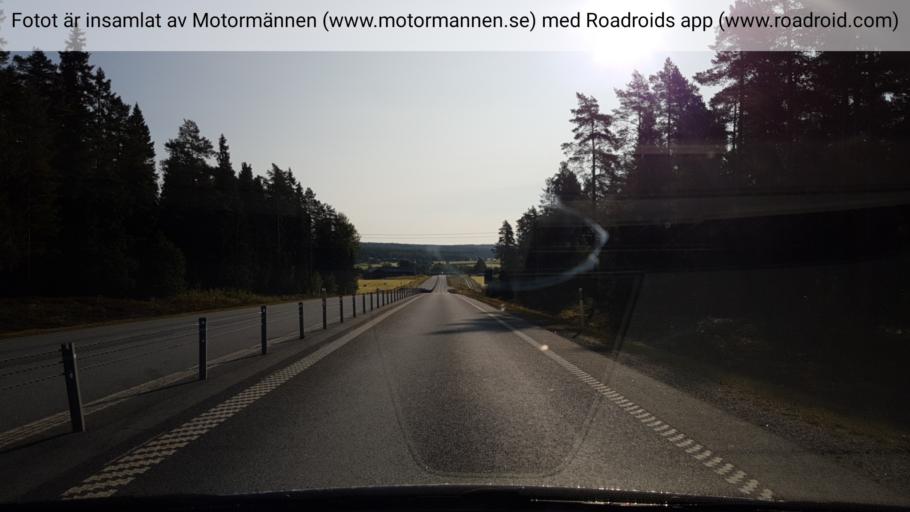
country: SE
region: Vaesterbotten
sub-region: Vannas Kommun
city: Vannasby
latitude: 63.8874
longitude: 20.0081
